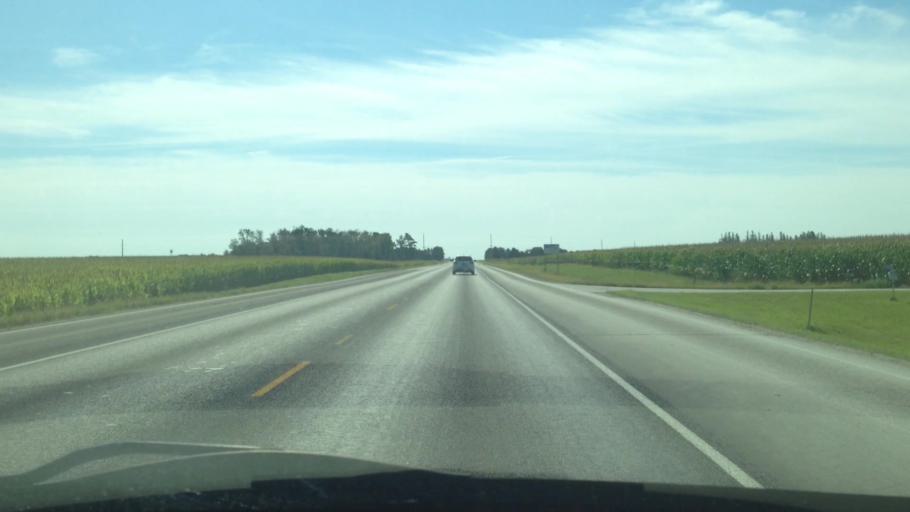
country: US
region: Minnesota
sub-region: Fillmore County
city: Harmony
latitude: 43.5442
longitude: -91.9534
